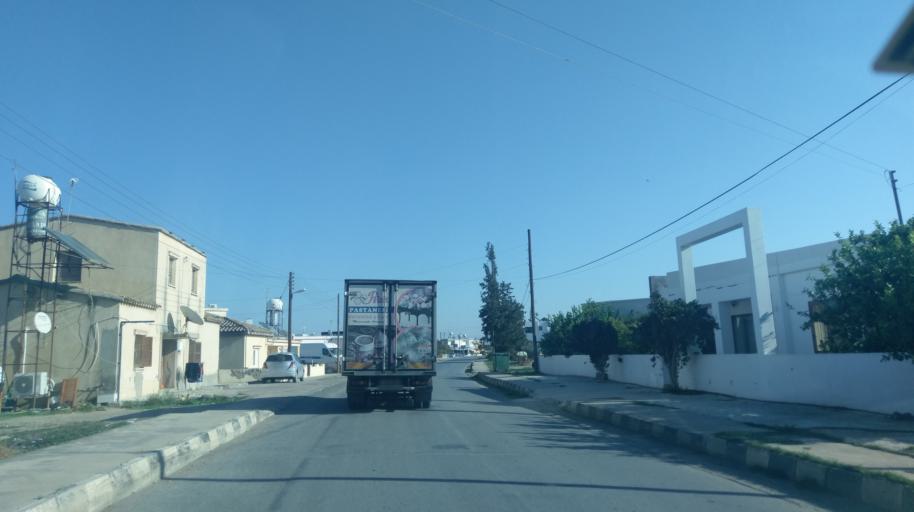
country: CY
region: Larnaka
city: Pergamos
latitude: 35.1092
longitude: 33.6871
